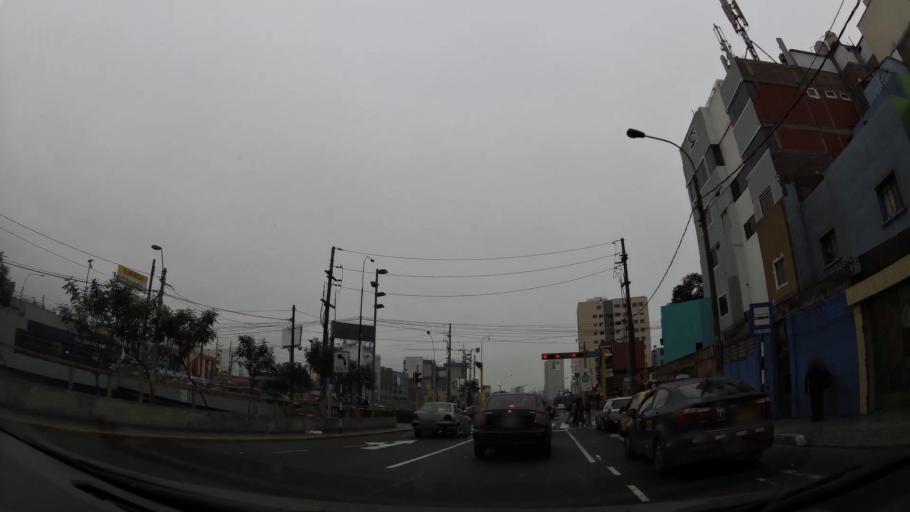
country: PE
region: Lima
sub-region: Lima
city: San Isidro
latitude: -12.1132
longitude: -77.0263
